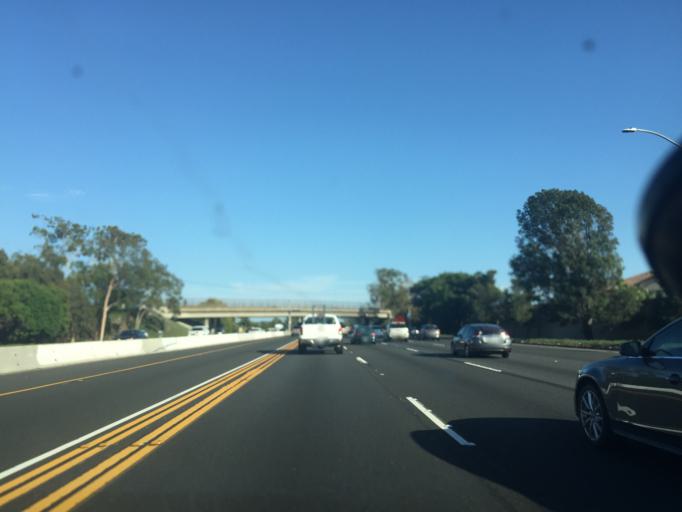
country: US
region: California
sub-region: Orange County
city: Fountain Valley
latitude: 33.7140
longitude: -117.9649
